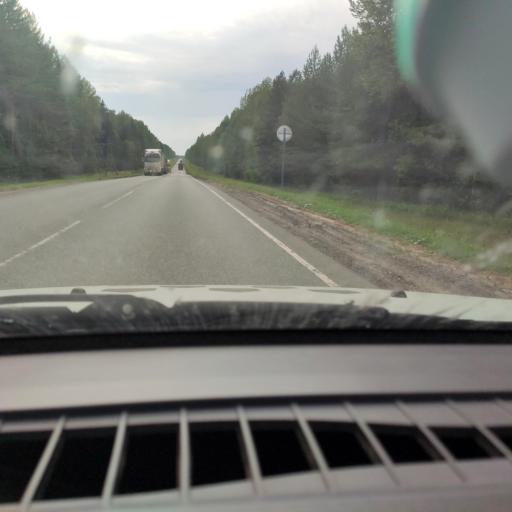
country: RU
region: Kirov
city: Belorechensk
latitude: 58.8077
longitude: 52.4578
